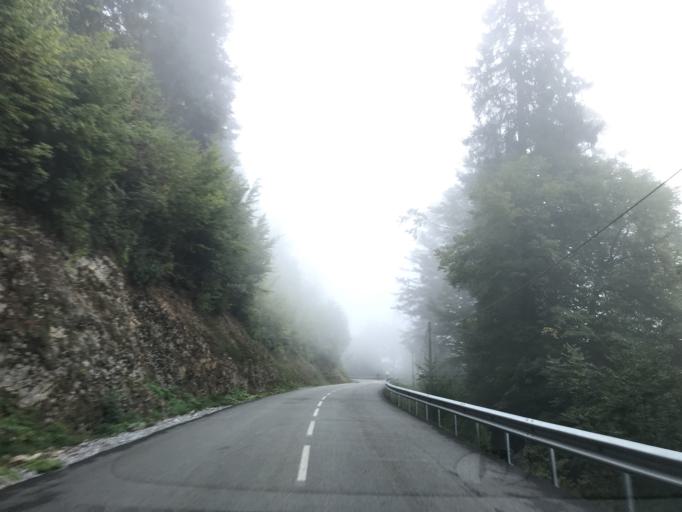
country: FR
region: Rhone-Alpes
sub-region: Departement de la Haute-Savoie
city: Talloires
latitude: 45.8132
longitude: 6.2424
